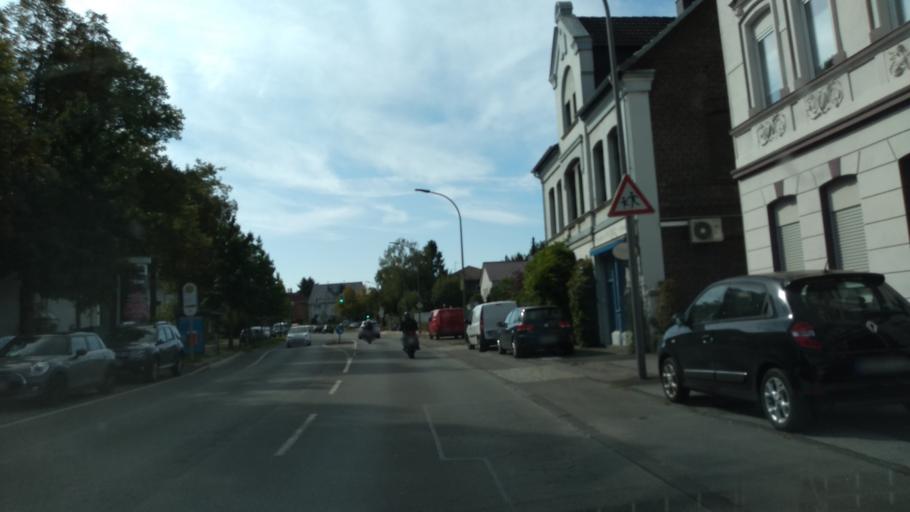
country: DE
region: North Rhine-Westphalia
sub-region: Regierungsbezirk Arnsberg
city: Bochum
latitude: 51.4548
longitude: 7.2009
